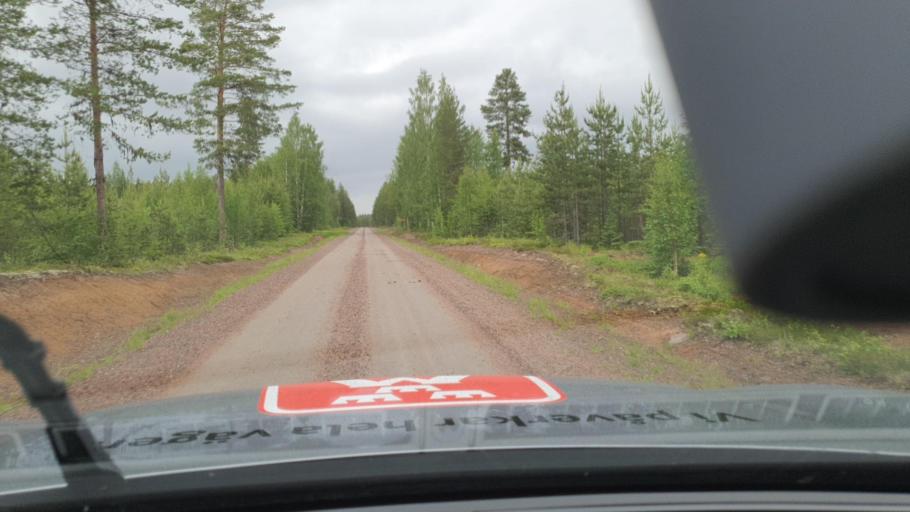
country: SE
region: Norrbotten
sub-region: Overkalix Kommun
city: OEverkalix
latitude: 66.6172
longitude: 22.7304
